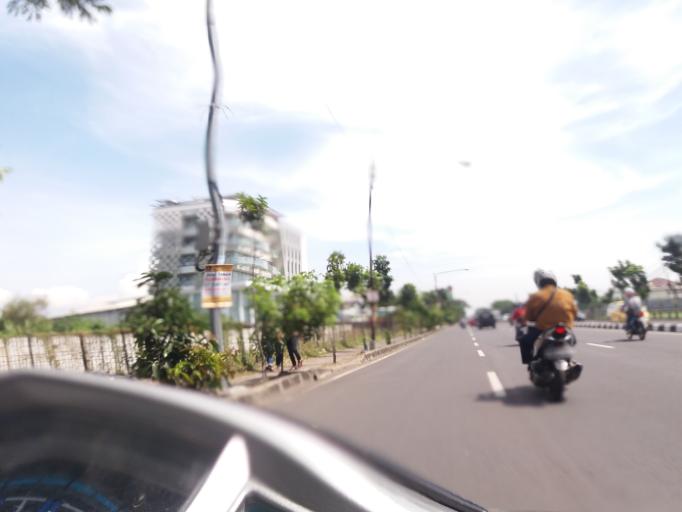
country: ID
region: West Java
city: Bandung
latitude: -6.9490
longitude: 107.6172
